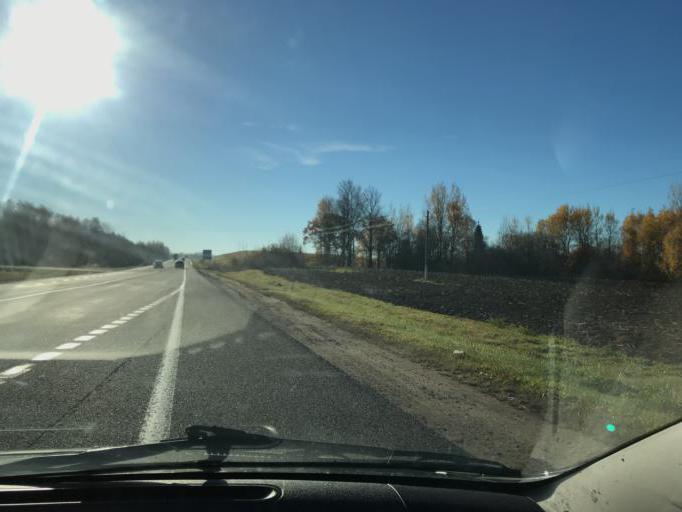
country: BY
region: Vitebsk
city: Vitebsk
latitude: 55.0968
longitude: 30.3008
